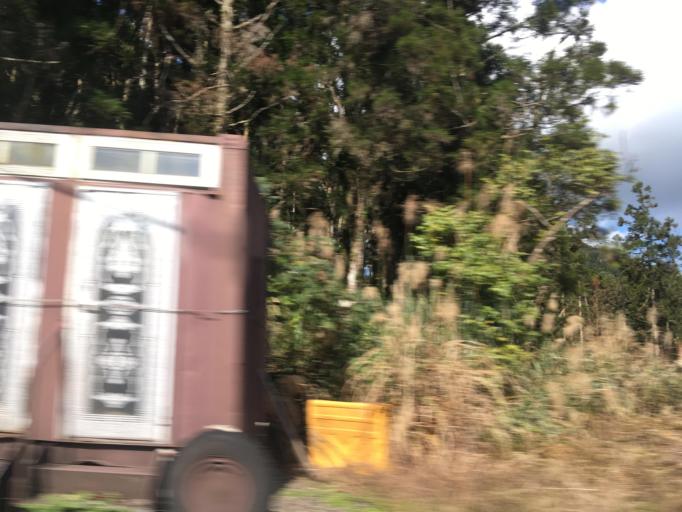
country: TW
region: Taiwan
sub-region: Yilan
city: Yilan
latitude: 24.7547
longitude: 121.6372
